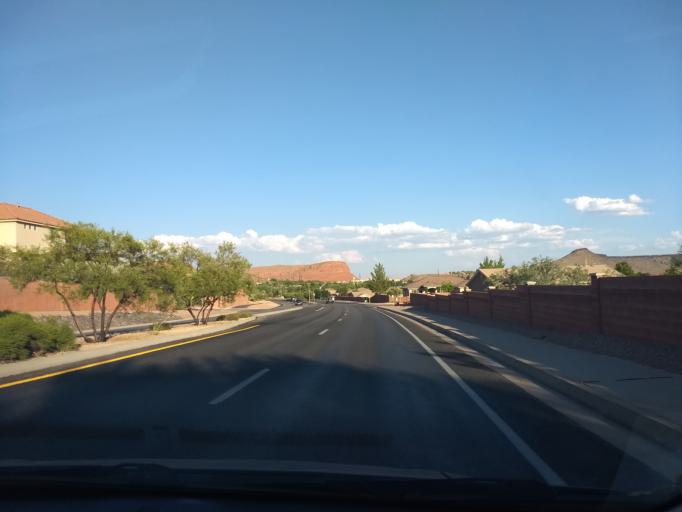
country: US
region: Utah
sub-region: Washington County
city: Santa Clara
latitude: 37.1351
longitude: -113.6162
